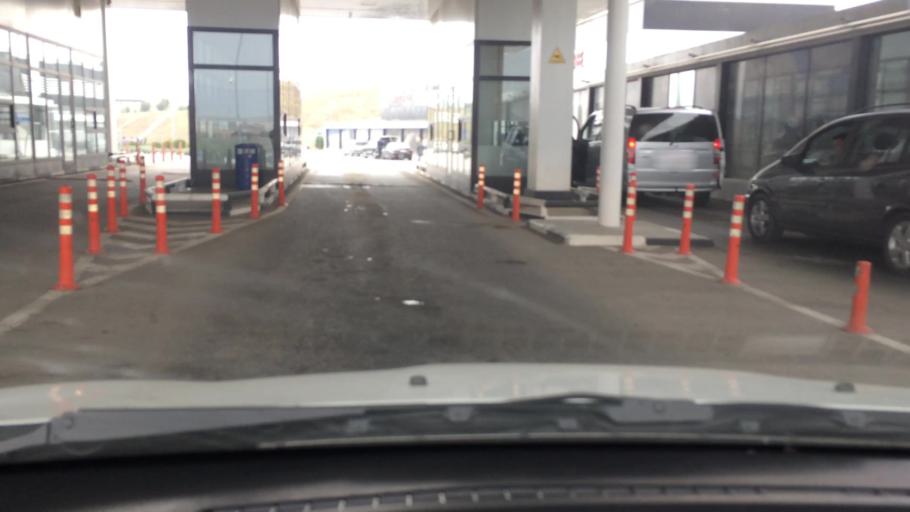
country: AM
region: Tavush
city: Bagratashen
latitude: 41.2278
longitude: 44.8307
